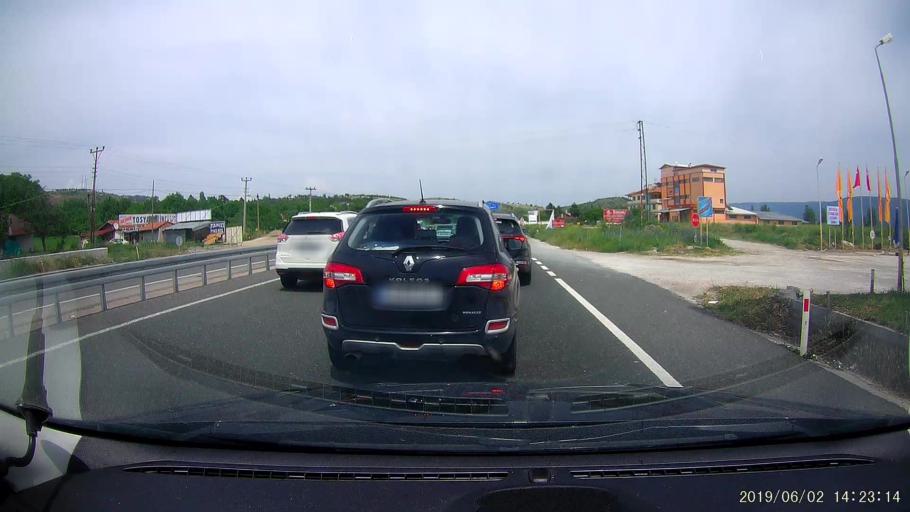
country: TR
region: Kastamonu
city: Tosya
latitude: 41.0008
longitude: 34.0277
